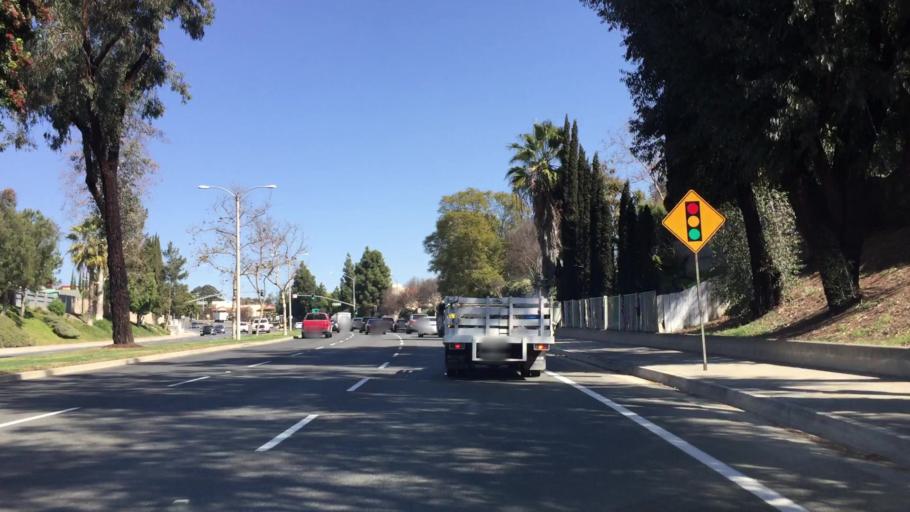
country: US
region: California
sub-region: Orange County
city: Mission Viejo
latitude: 33.5980
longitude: -117.6930
